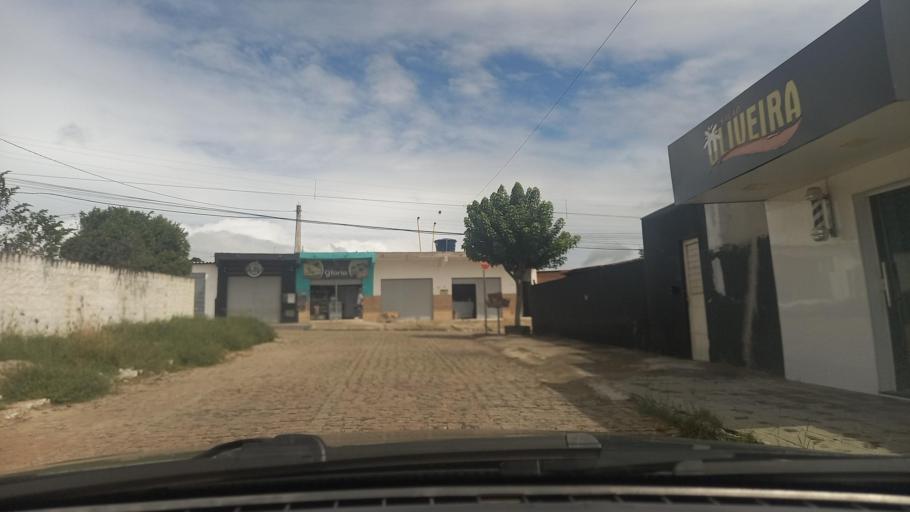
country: BR
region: Bahia
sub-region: Paulo Afonso
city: Paulo Afonso
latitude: -9.3433
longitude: -38.2594
